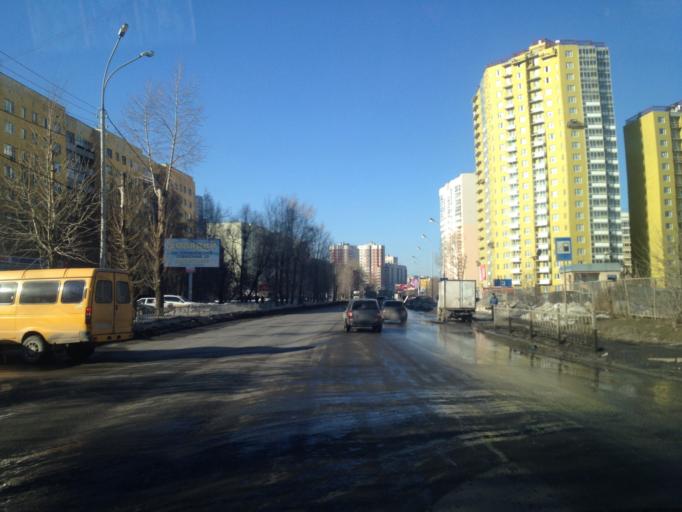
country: RU
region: Sverdlovsk
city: Yekaterinburg
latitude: 56.9043
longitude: 60.6228
